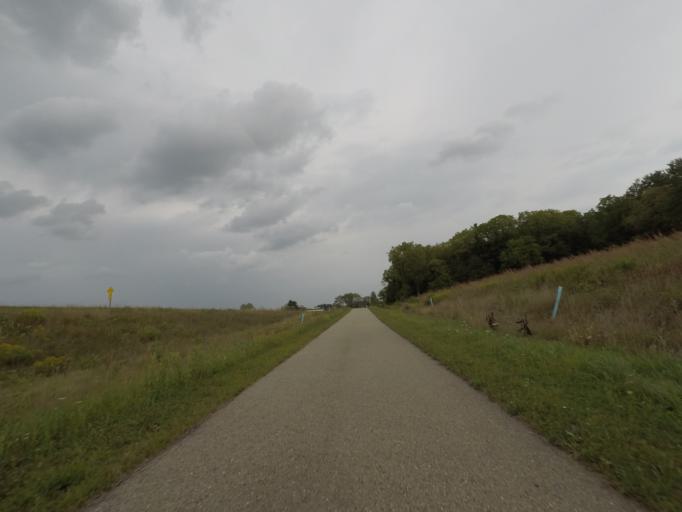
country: US
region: Wisconsin
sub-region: Jefferson County
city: Jefferson
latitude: 42.9862
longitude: -88.8293
